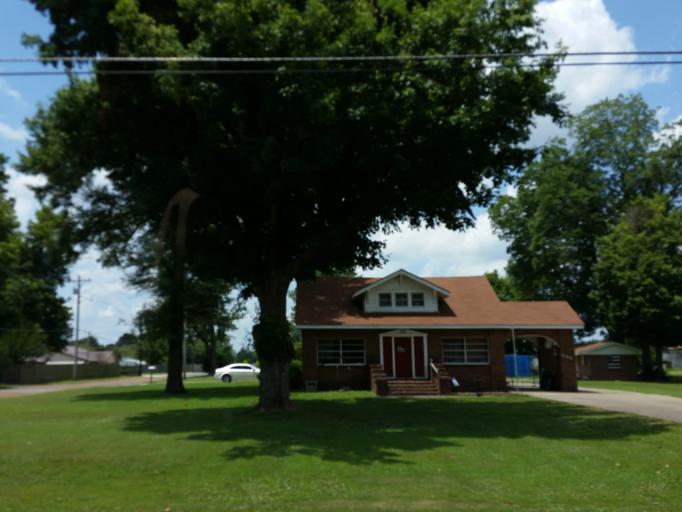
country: US
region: Tennessee
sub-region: Lake County
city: Ridgely
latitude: 36.2716
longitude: -89.4780
